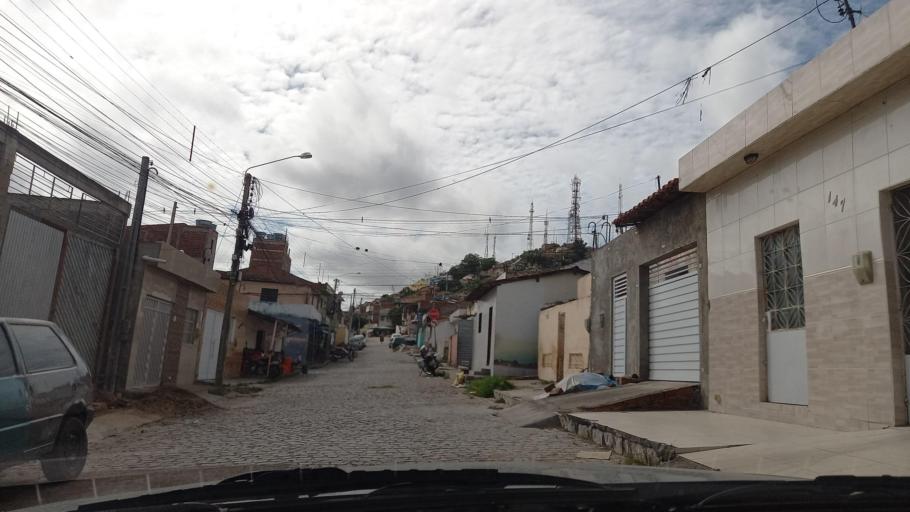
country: BR
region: Pernambuco
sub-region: Caruaru
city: Caruaru
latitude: -8.2840
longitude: -35.9815
